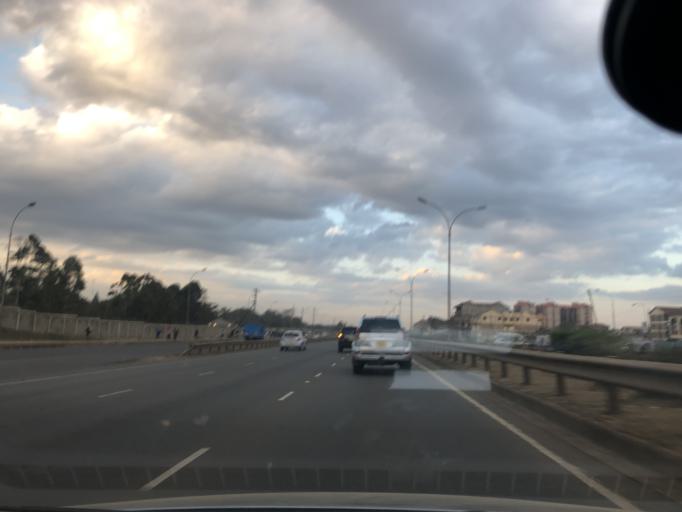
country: KE
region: Kiambu
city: Kiambu
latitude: -1.1964
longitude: 36.9238
